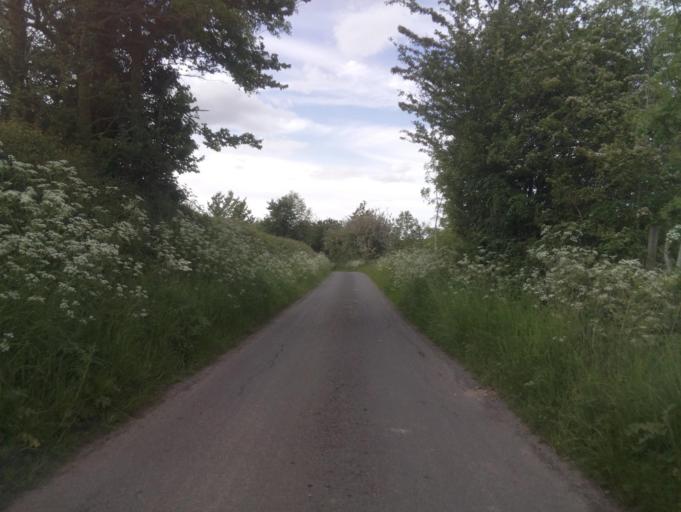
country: GB
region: England
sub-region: Gloucestershire
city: Moreton in Marsh
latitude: 52.0297
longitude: -1.7184
